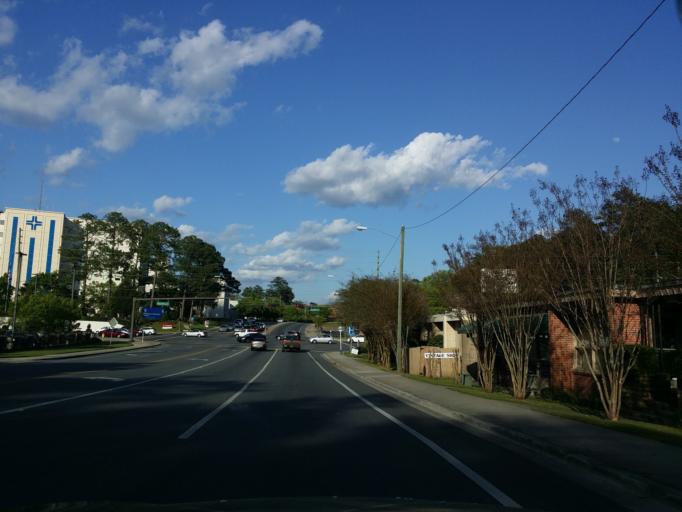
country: US
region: Florida
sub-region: Leon County
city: Tallahassee
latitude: 30.4550
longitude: -84.2635
